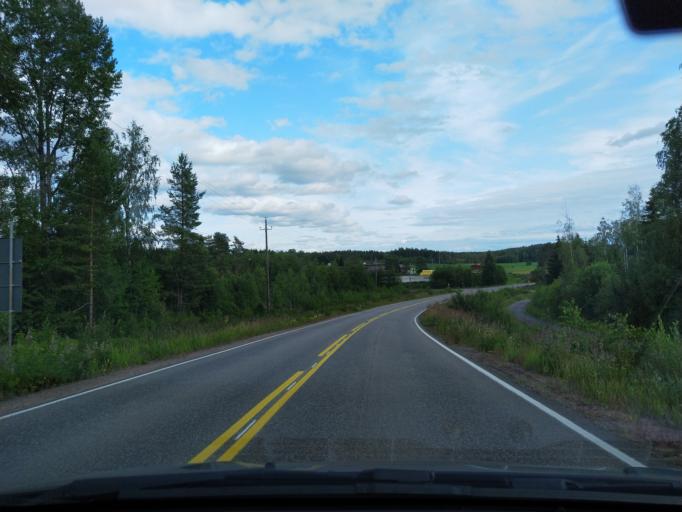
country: FI
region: Kymenlaakso
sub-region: Kouvola
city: Kouvola
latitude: 61.0637
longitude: 26.8335
